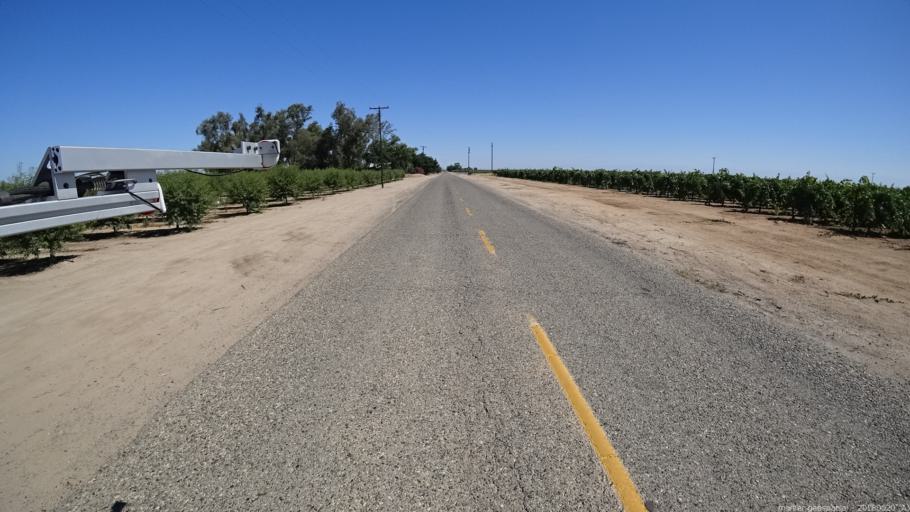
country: US
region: California
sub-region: Madera County
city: Parkwood
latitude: 36.8864
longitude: -120.0195
